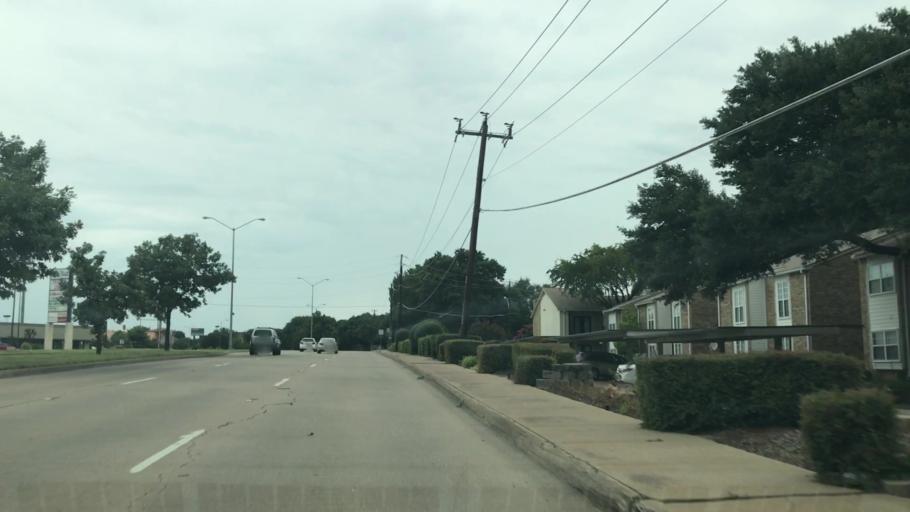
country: US
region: Texas
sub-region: Dallas County
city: Addison
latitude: 32.9516
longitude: -96.8002
